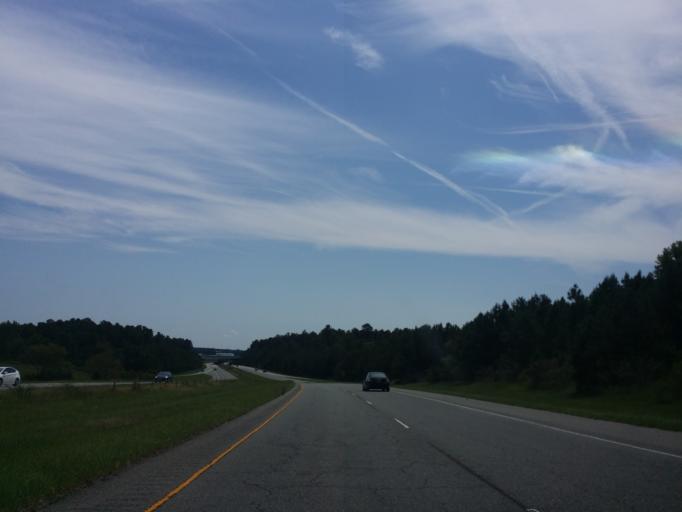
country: US
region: North Carolina
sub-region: Wake County
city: Morrisville
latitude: 35.8898
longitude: -78.8134
